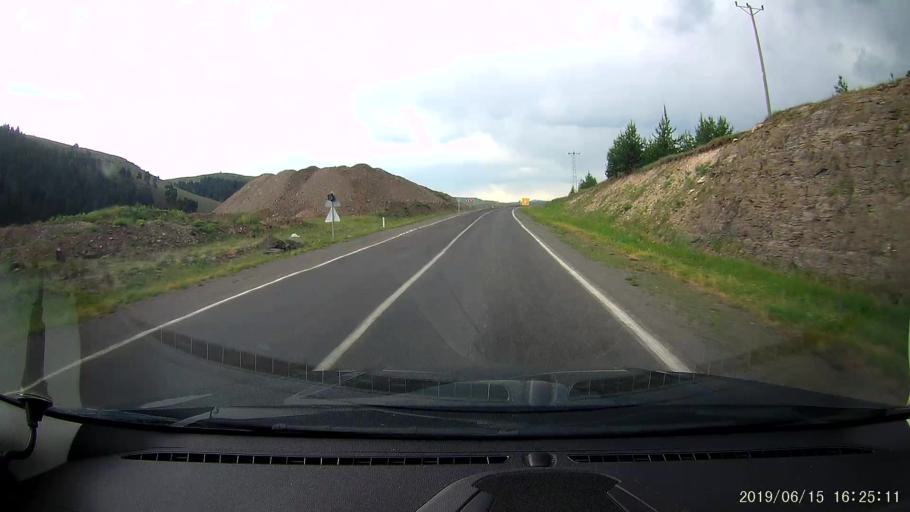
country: TR
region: Ardahan
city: Hanak
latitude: 41.1569
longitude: 42.8713
